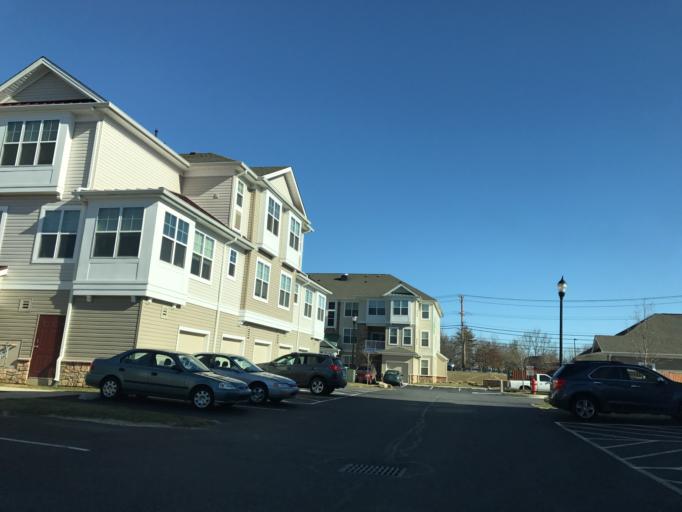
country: US
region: Maryland
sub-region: Harford County
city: Riverside
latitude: 39.4869
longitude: -76.2386
